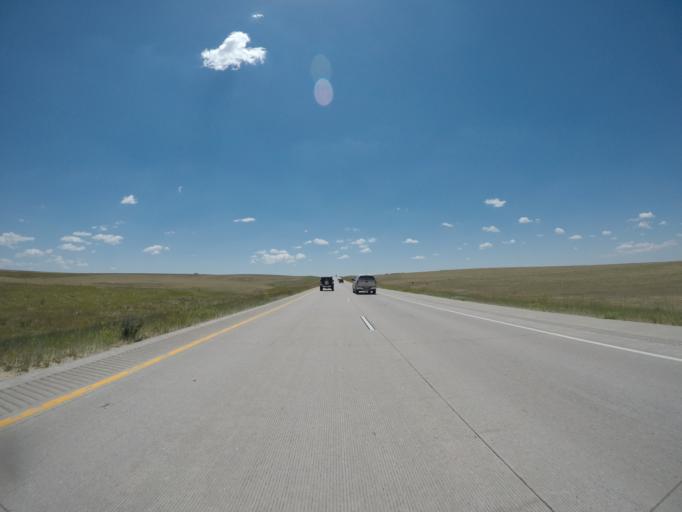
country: US
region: Colorado
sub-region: Lincoln County
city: Limon
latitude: 39.3991
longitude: -103.8984
